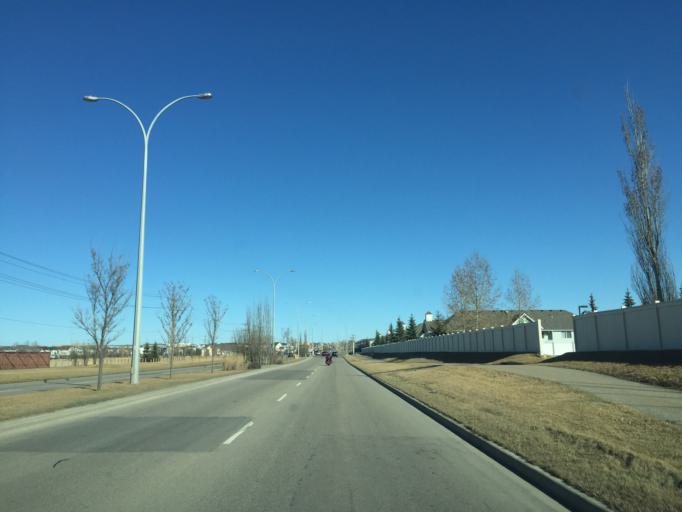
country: CA
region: Alberta
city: Airdrie
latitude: 51.2999
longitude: -114.0298
